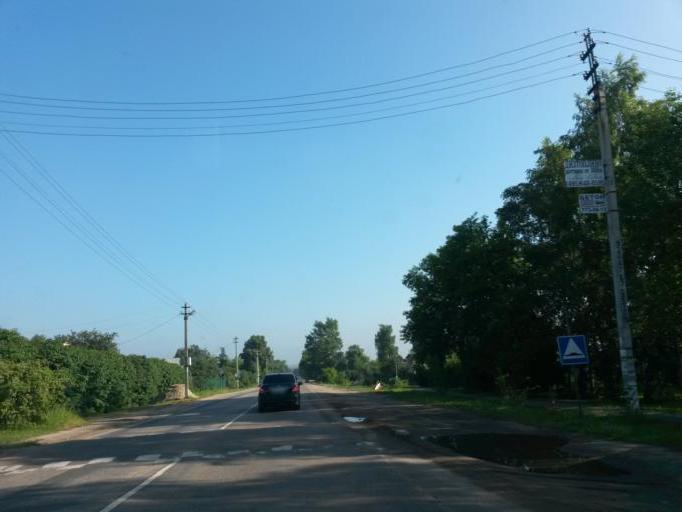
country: RU
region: Moskovskaya
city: Yam
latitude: 55.4782
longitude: 37.7524
